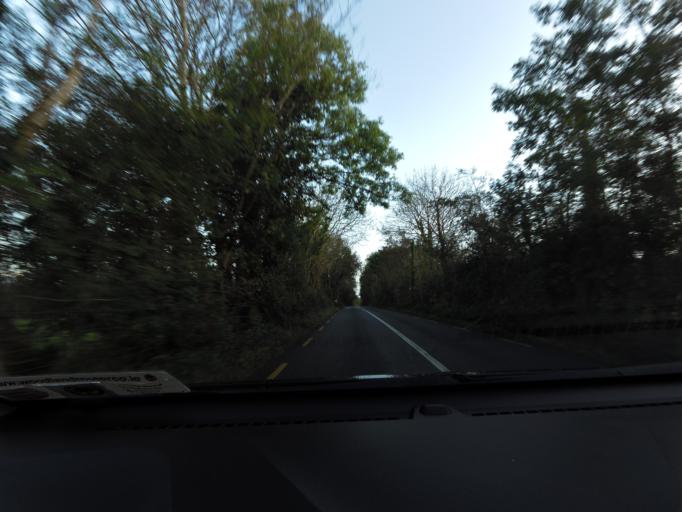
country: IE
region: Connaught
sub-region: County Galway
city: Tuam
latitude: 53.5053
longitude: -8.6099
